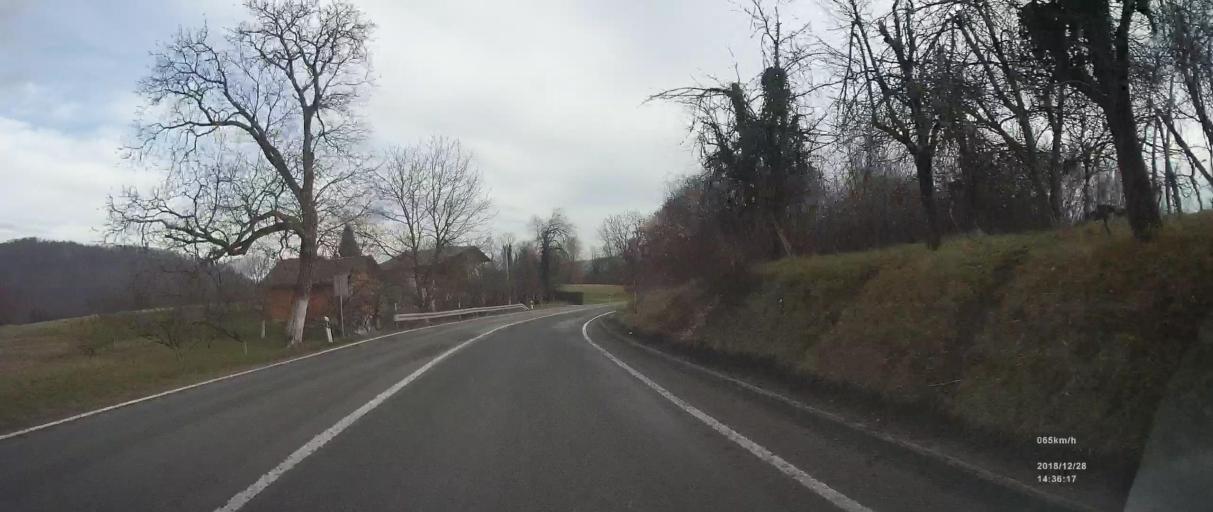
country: HR
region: Primorsko-Goranska
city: Vrbovsko
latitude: 45.4233
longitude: 15.1946
